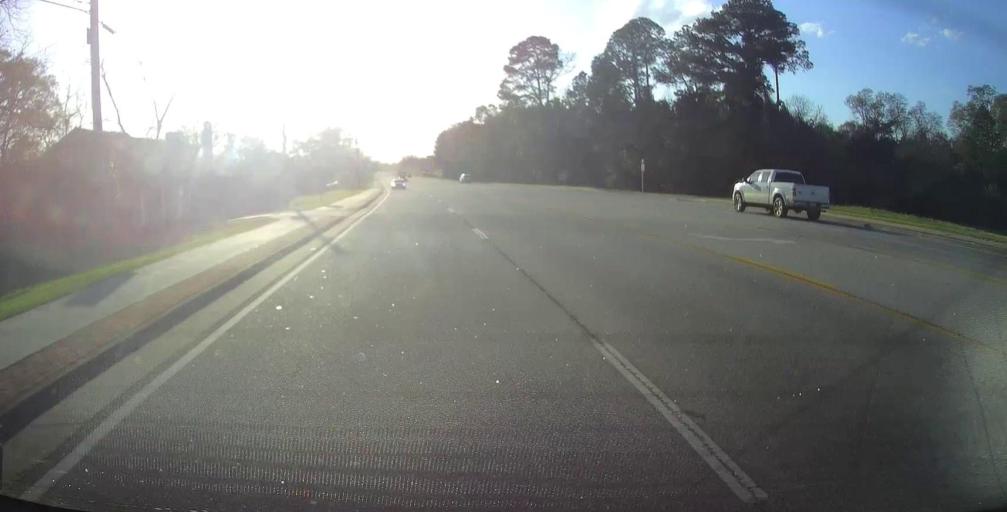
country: US
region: Georgia
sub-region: Evans County
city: Claxton
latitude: 32.1610
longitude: -81.9187
